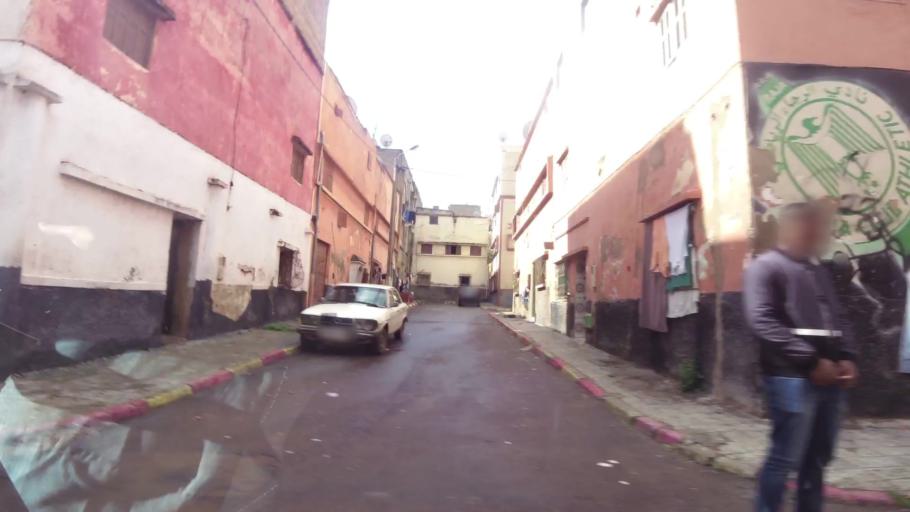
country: MA
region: Grand Casablanca
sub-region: Nouaceur
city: Bouskoura
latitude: 33.5074
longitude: -7.6582
